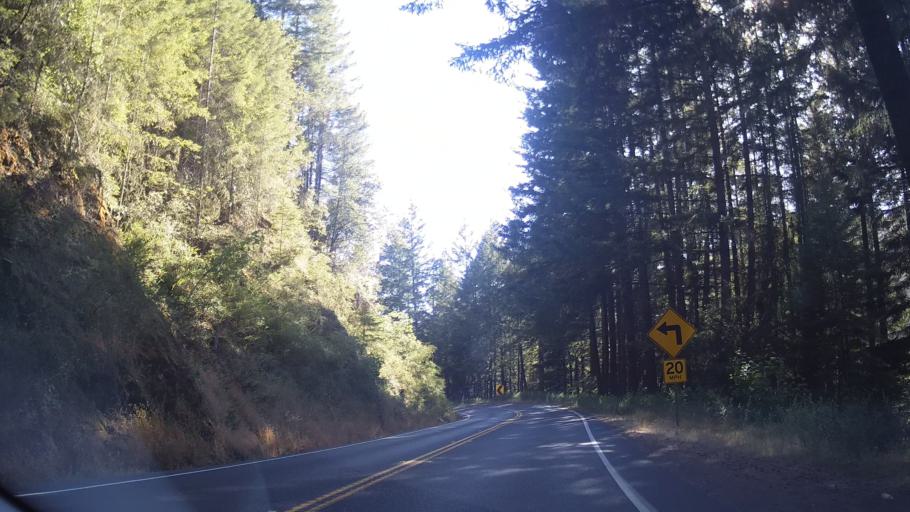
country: US
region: California
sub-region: Mendocino County
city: Brooktrails
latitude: 39.3721
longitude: -123.4963
